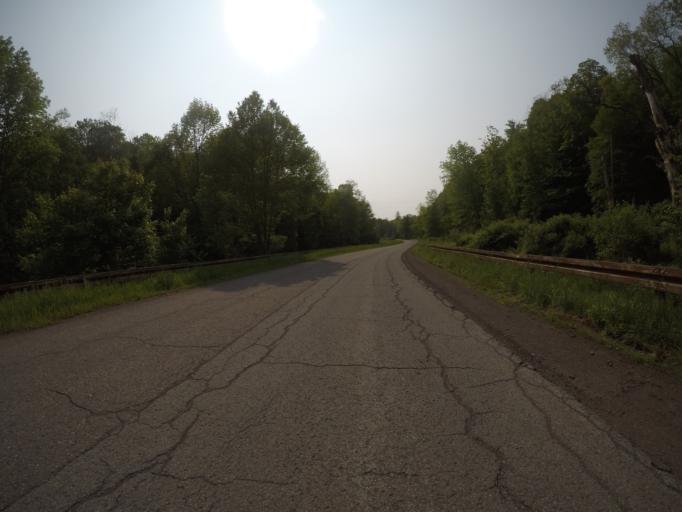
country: US
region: New York
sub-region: Sullivan County
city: Livingston Manor
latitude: 42.0834
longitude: -74.7848
